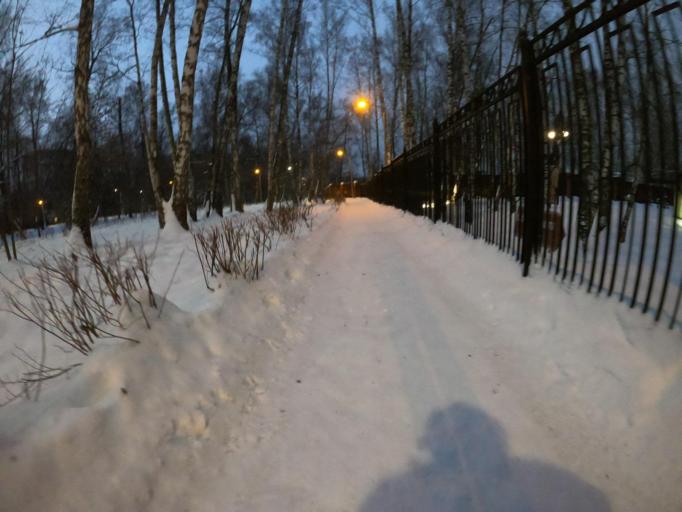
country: RU
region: Moskovskaya
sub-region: Podol'skiy Rayon
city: Podol'sk
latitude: 55.4182
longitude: 37.5247
